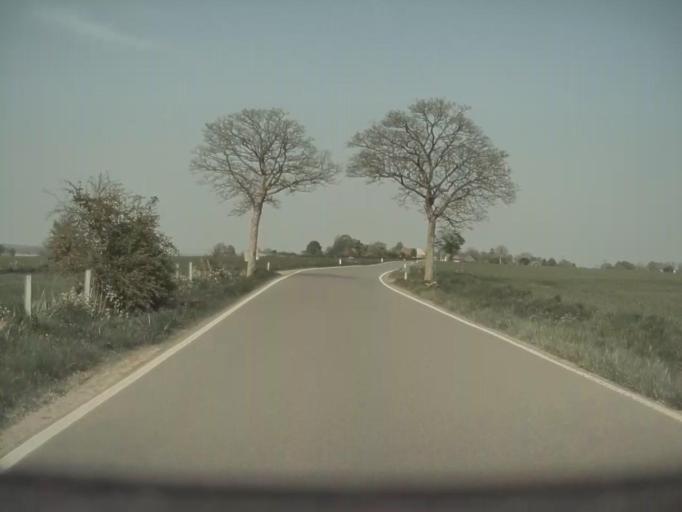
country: BE
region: Wallonia
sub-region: Province de Namur
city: Somme-Leuze
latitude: 50.3478
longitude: 5.2989
